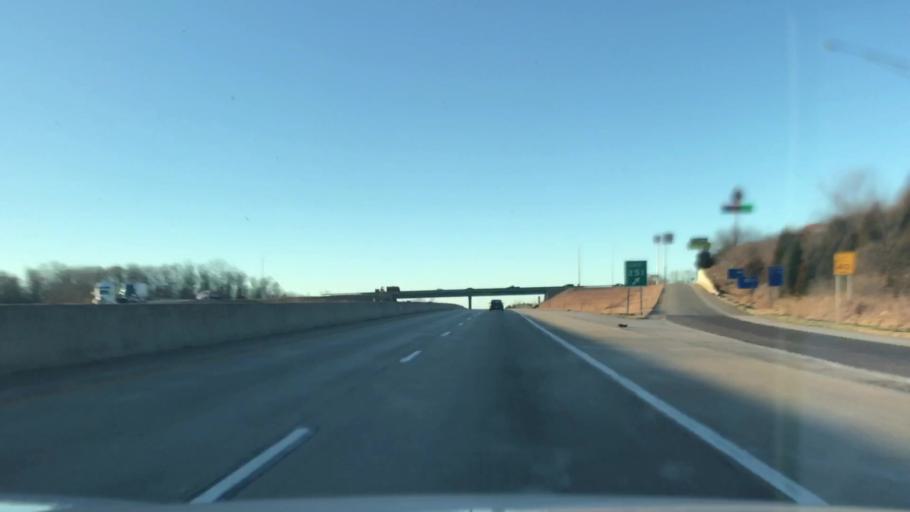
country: US
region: Missouri
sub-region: Franklin County
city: Gray Summit
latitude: 38.4769
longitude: -90.8490
